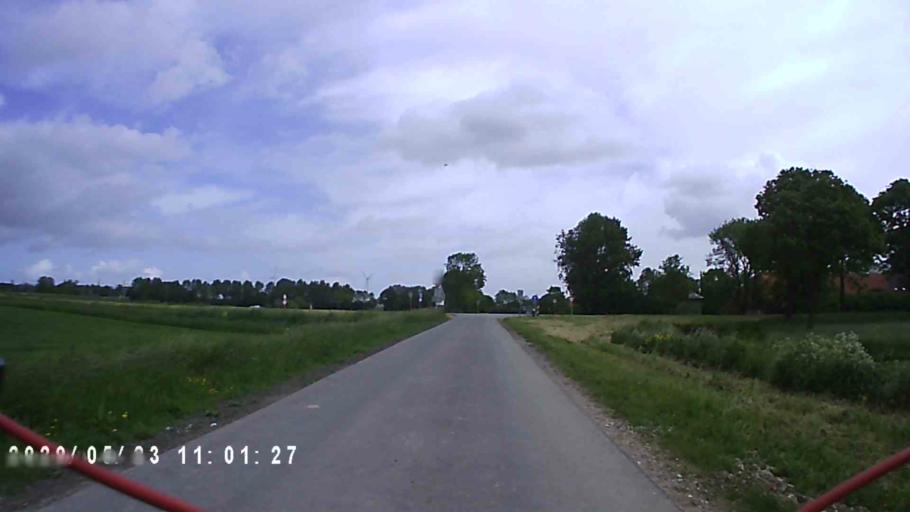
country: NL
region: Groningen
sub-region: Gemeente Delfzijl
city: Delfzijl
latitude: 53.3092
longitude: 6.9440
